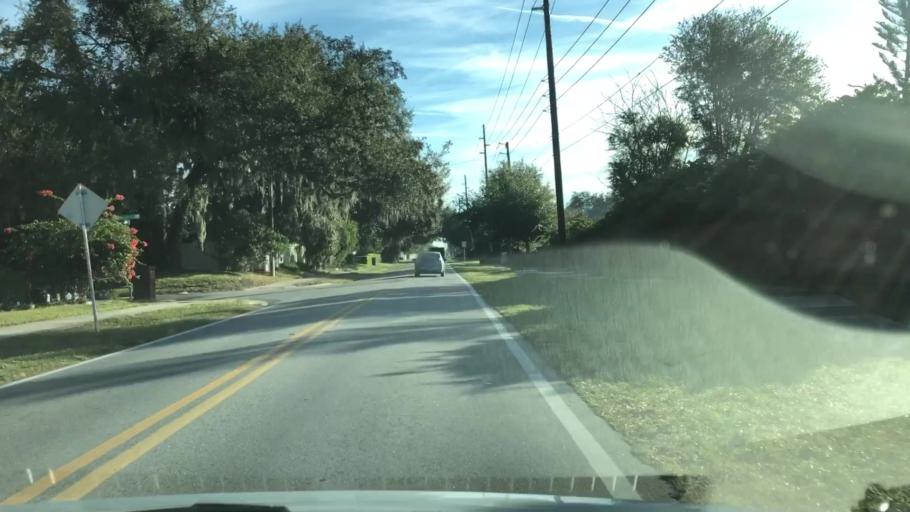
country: US
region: Florida
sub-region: Orange County
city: Conway
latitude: 28.4950
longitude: -81.3375
